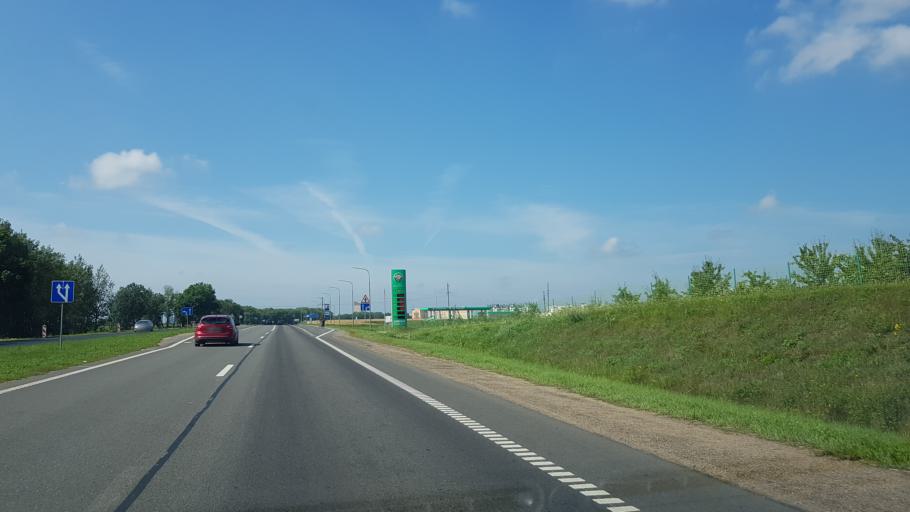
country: BY
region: Minsk
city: Dzyarzhynsk
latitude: 53.6957
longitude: 27.1772
